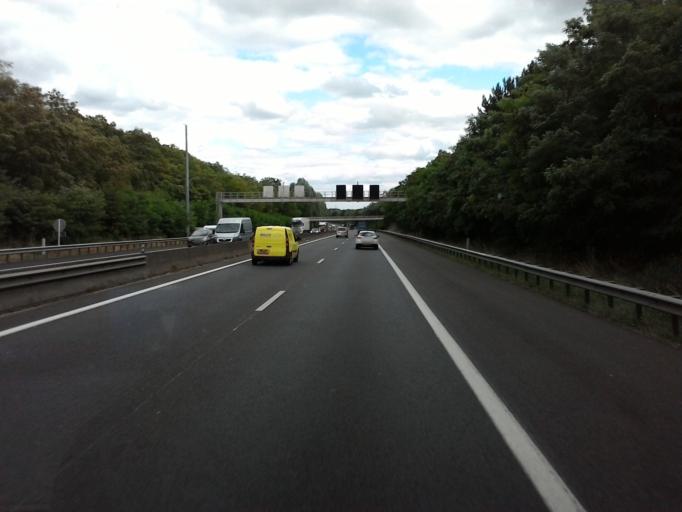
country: LU
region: Luxembourg
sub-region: Canton de Capellen
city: Mamer
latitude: 49.6354
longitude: 6.0280
